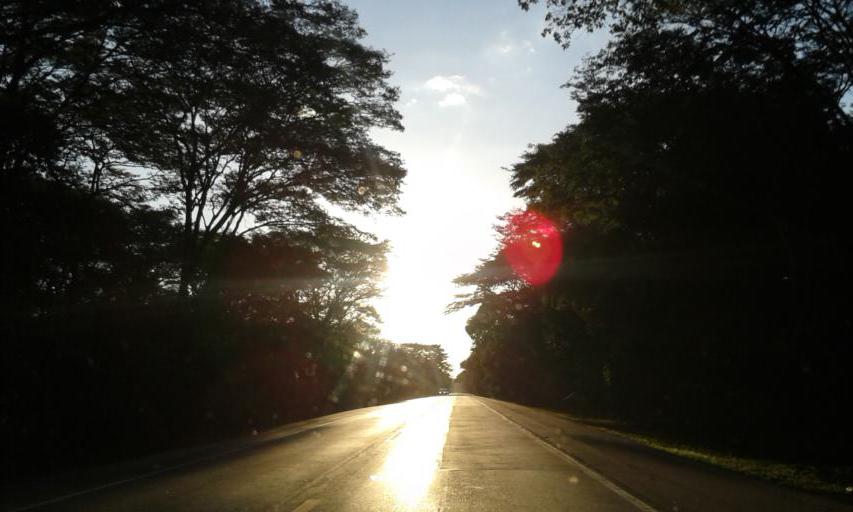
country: BR
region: Minas Gerais
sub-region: Bom Despacho
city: Bom Despacho
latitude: -19.7839
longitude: -45.4302
